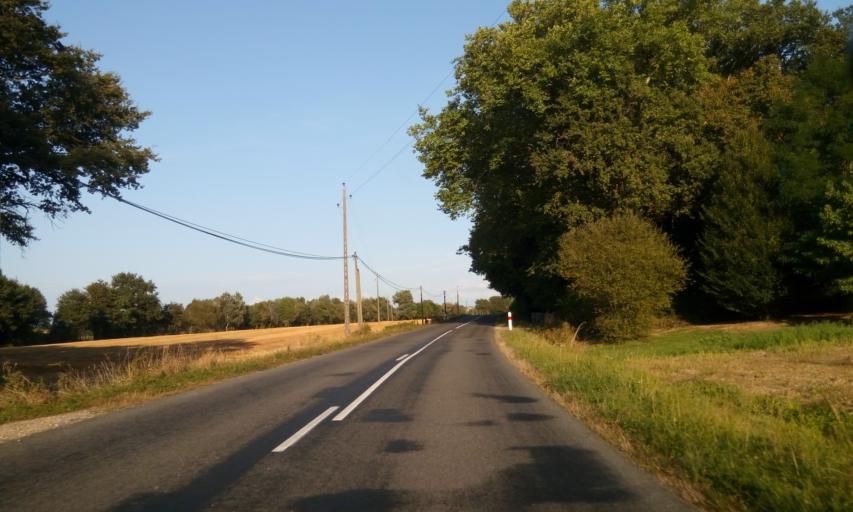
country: FR
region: Rhone-Alpes
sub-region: Departement de l'Ain
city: Chalamont
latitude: 45.9975
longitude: 5.1444
